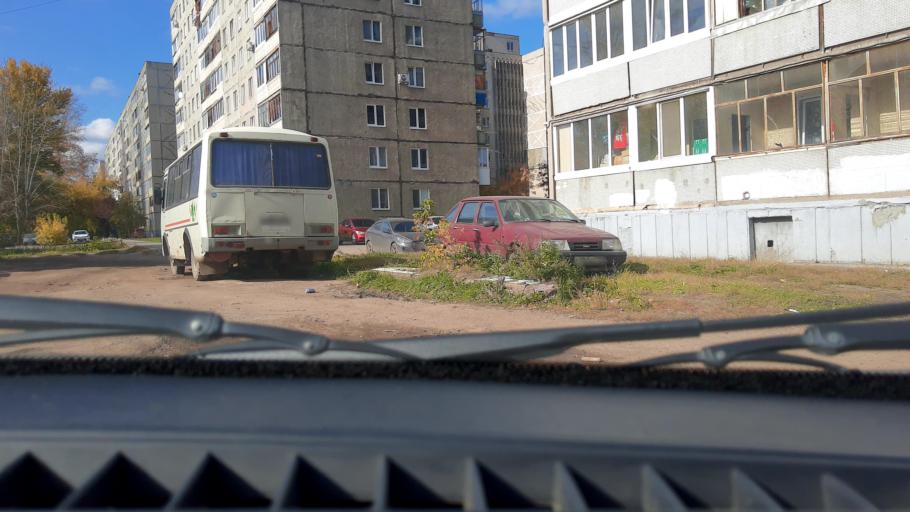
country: RU
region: Bashkortostan
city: Ufa
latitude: 54.7746
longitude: 56.1305
